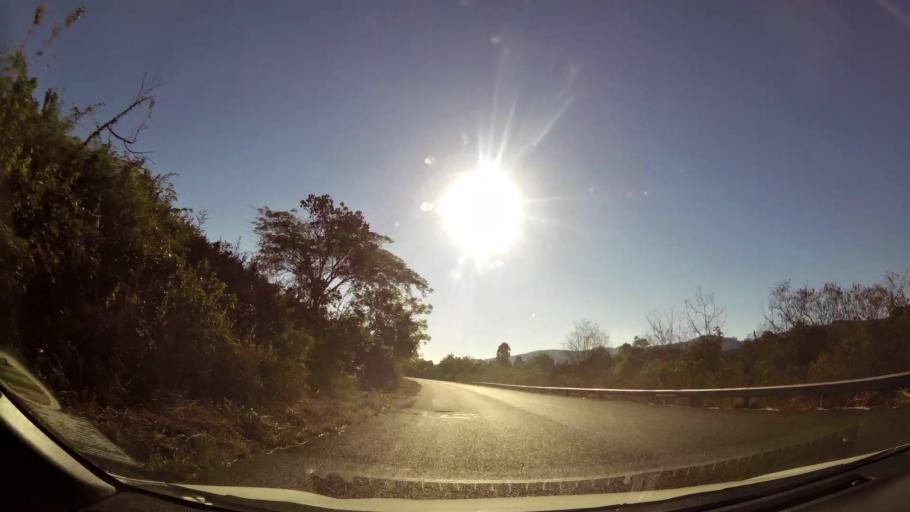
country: ZA
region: Limpopo
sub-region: Mopani District Municipality
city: Tzaneen
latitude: -23.9314
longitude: 30.0399
